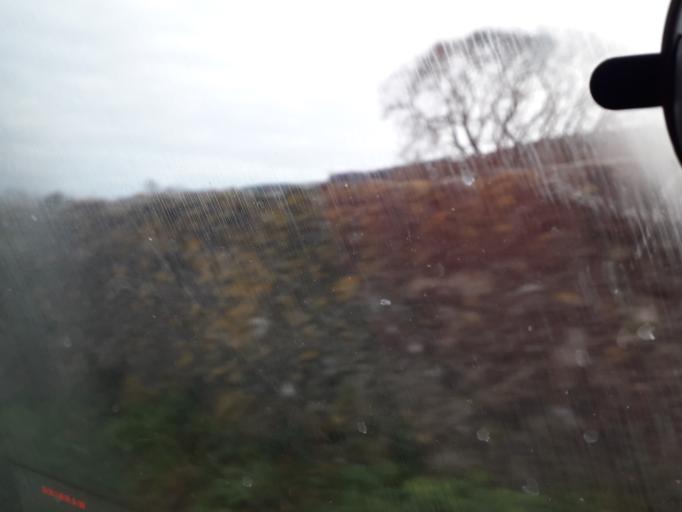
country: IE
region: Leinster
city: Ballyboden
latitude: 53.2645
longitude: -6.2868
